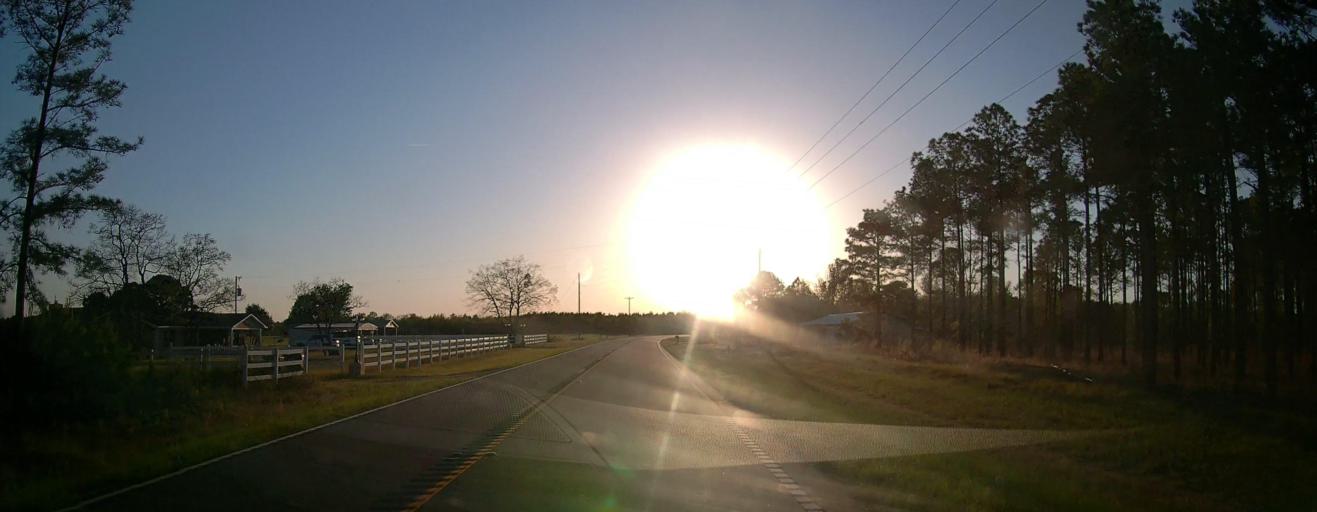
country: US
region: Georgia
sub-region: Talbot County
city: Talbotton
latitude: 32.5371
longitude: -84.5059
